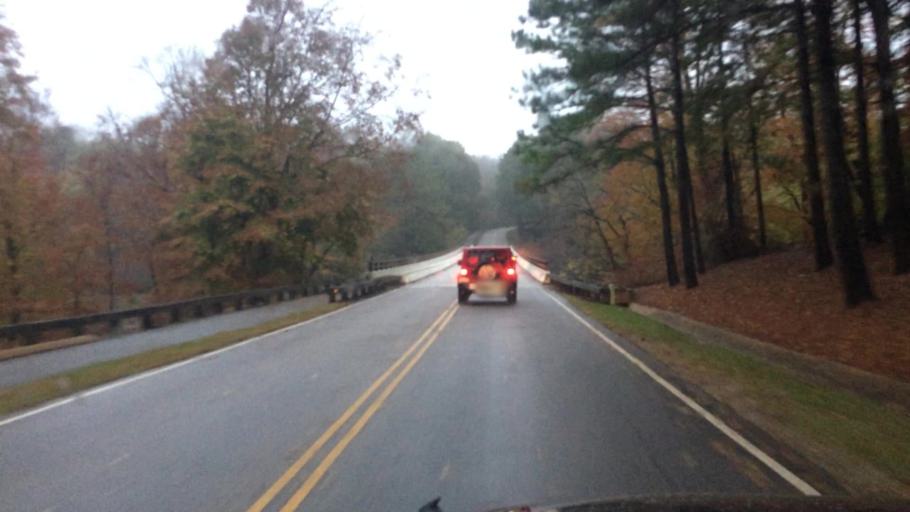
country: US
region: Virginia
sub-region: City of Williamsburg
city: Williamsburg
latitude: 37.2353
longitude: -76.6803
